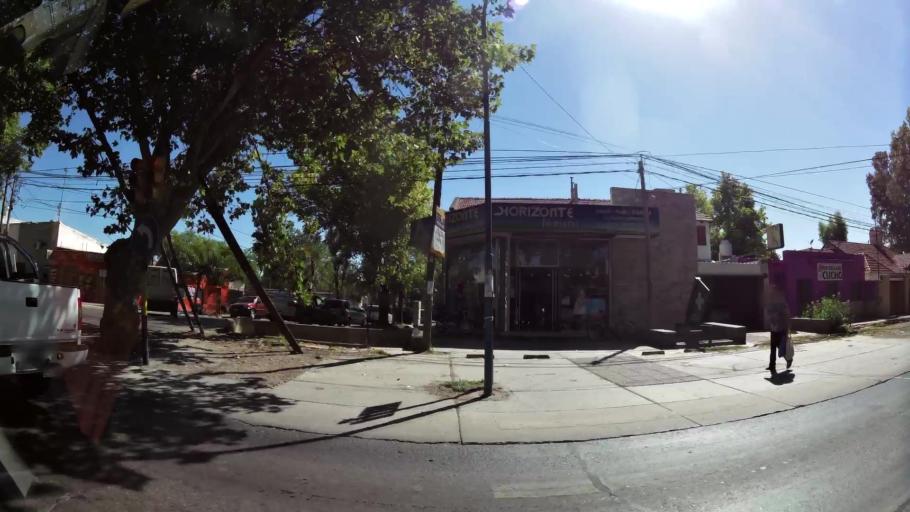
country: AR
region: Mendoza
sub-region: Departamento de Godoy Cruz
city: Godoy Cruz
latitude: -32.9427
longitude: -68.8211
